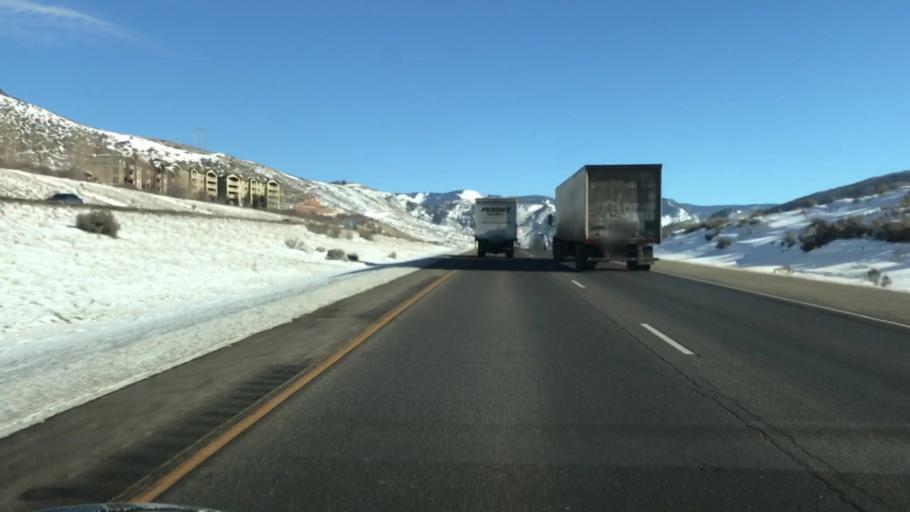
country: US
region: Colorado
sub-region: Eagle County
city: Avon
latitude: 39.6319
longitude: -106.5077
